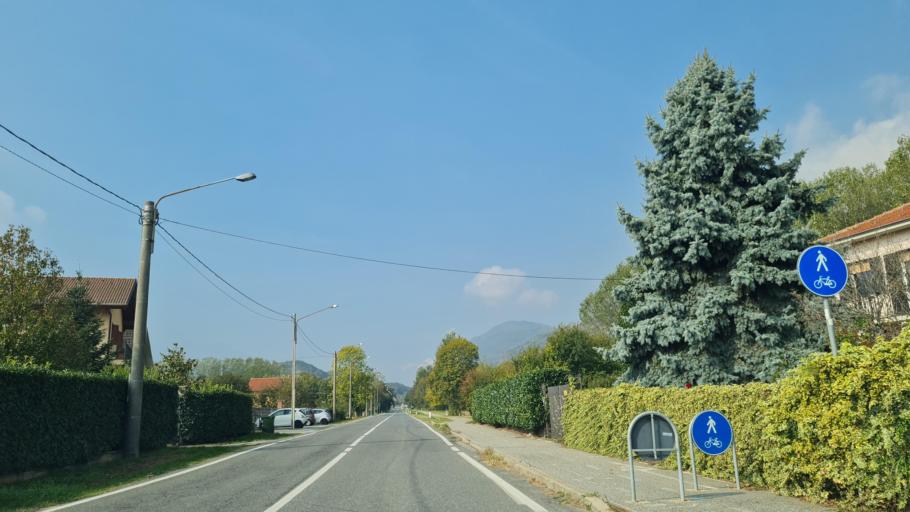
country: IT
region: Piedmont
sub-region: Provincia di Torino
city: Caprie
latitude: 45.1182
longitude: 7.3487
